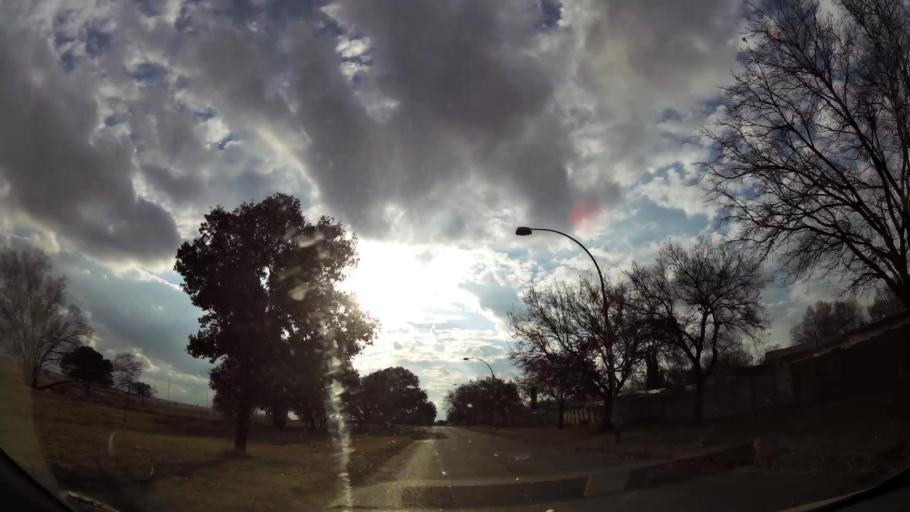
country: ZA
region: Orange Free State
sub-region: Fezile Dabi District Municipality
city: Sasolburg
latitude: -26.8247
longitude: 27.8127
